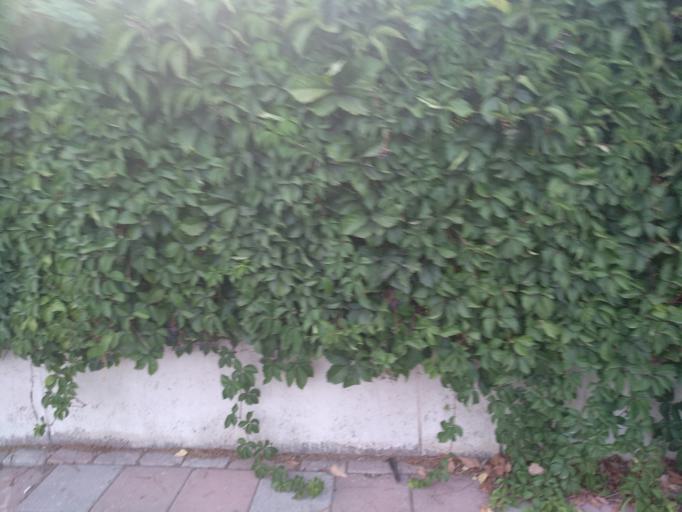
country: TR
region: Antalya
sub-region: Kemer
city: Goeynuek
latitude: 36.6623
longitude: 30.5592
